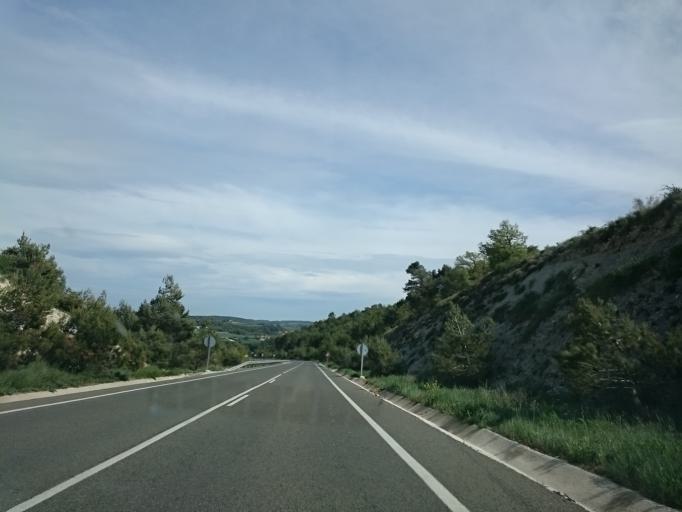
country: ES
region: Catalonia
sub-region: Provincia de Tarragona
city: Santa Coloma de Queralt
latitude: 41.5606
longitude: 1.3997
